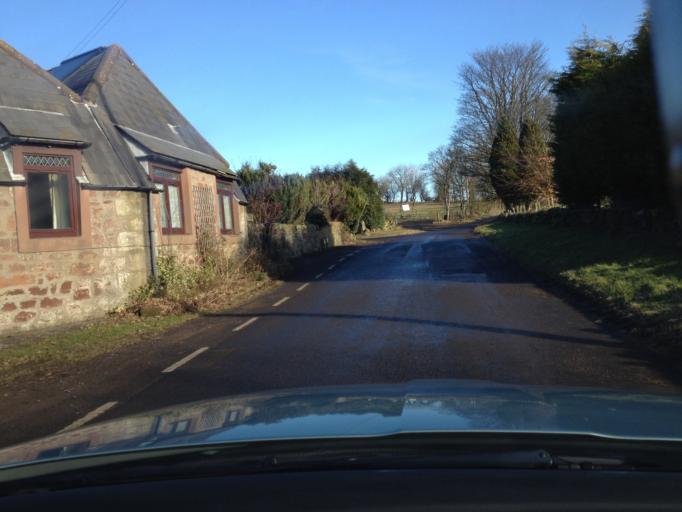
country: GB
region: Scotland
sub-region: Perth and Kinross
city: Milnathort
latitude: 56.2391
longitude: -3.4036
